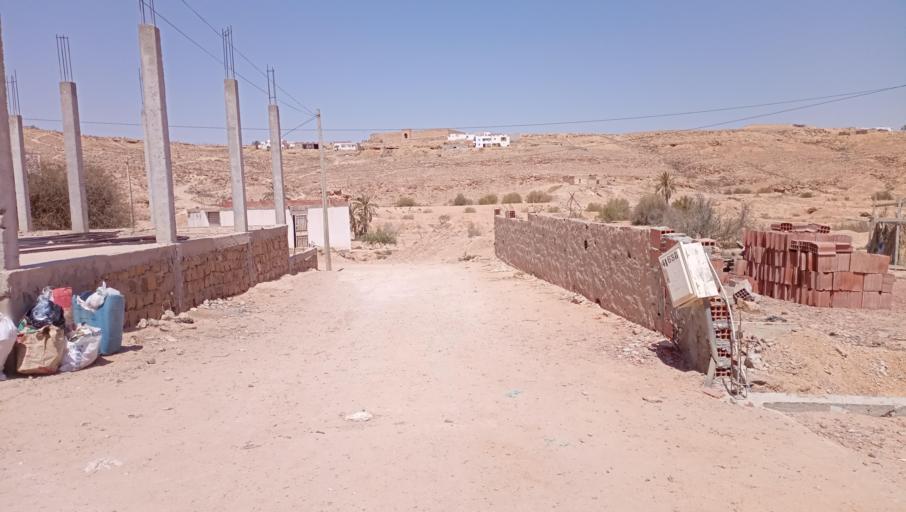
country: TN
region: Tataouine
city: Tataouine
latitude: 32.8457
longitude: 10.4723
